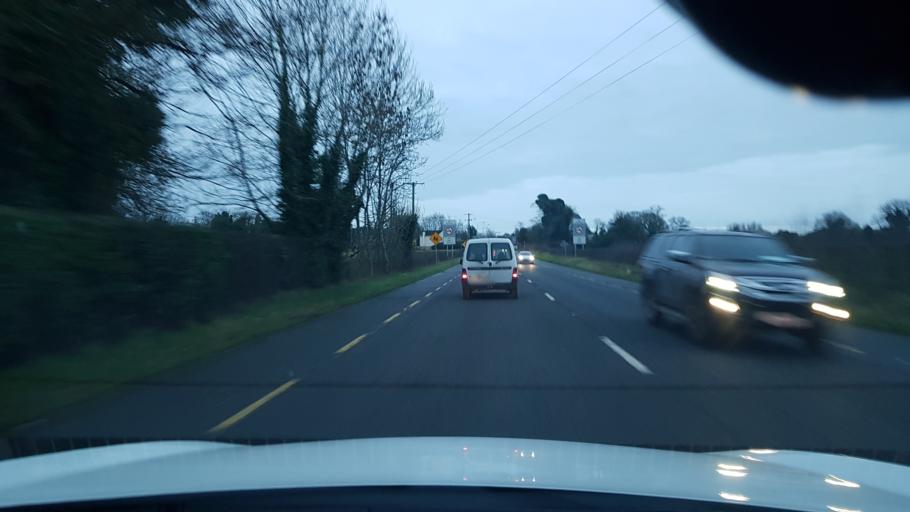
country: IE
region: Leinster
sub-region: An Mhi
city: Dunshaughlin
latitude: 53.4799
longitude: -6.5073
